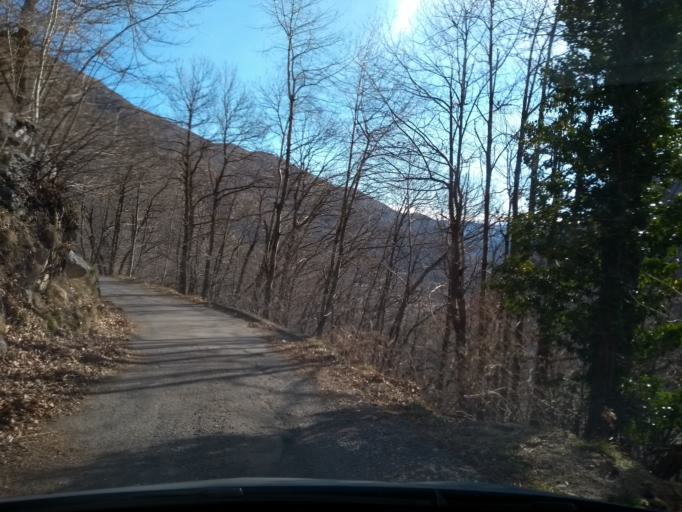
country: IT
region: Piedmont
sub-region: Provincia di Torino
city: Cantoira
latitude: 45.3471
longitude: 7.3800
